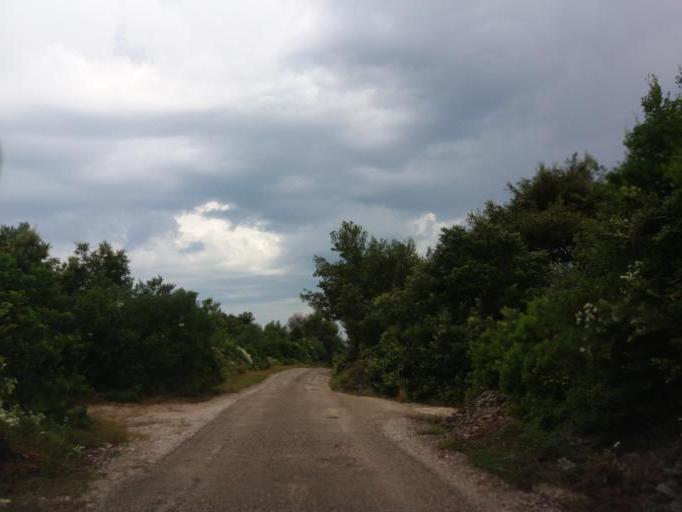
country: HR
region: Zadarska
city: Sali
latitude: 43.9065
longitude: 15.1414
